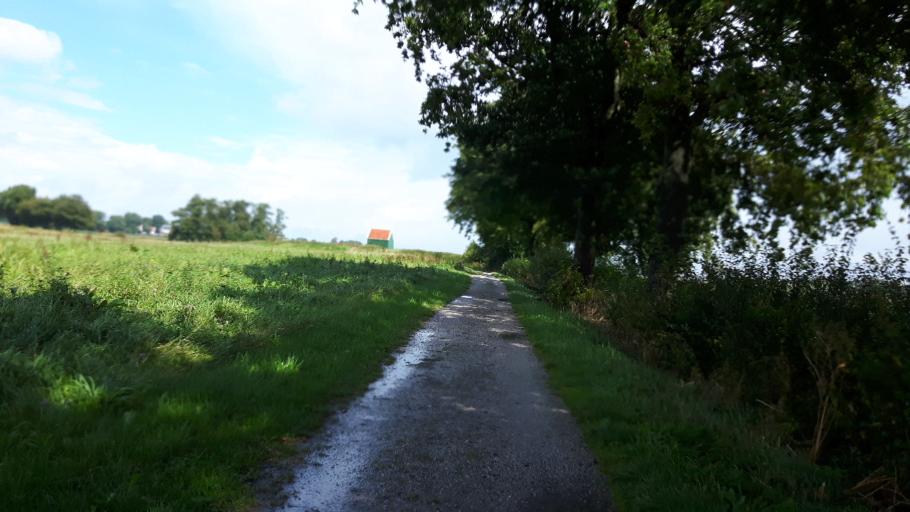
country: NL
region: Flevoland
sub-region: Gemeente Noordoostpolder
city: Ens
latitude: 52.6268
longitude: 5.7770
